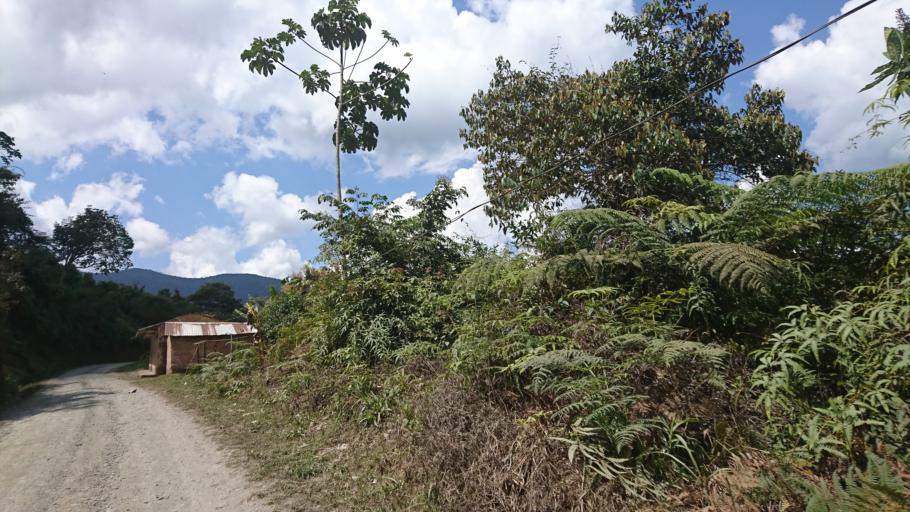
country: BO
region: La Paz
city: Coroico
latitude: -16.0774
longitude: -67.7810
